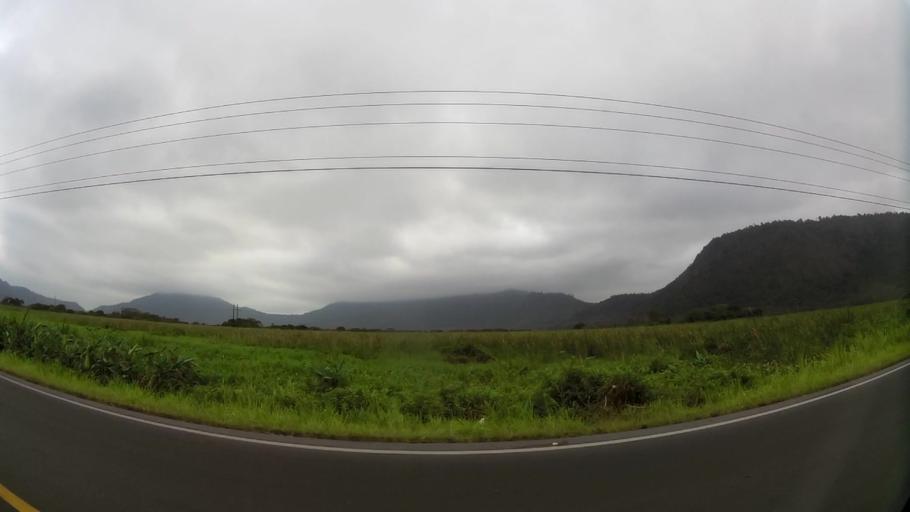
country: EC
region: Guayas
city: Naranjal
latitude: -2.4355
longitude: -79.6266
